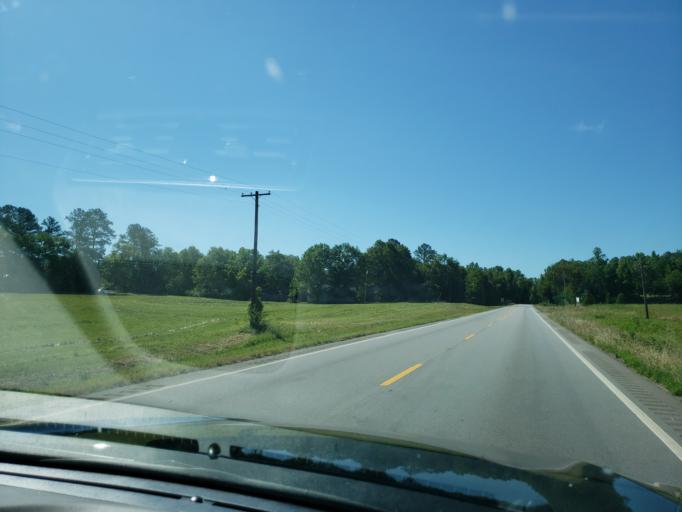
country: US
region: Alabama
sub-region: Cleburne County
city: Heflin
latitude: 33.5505
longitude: -85.6513
